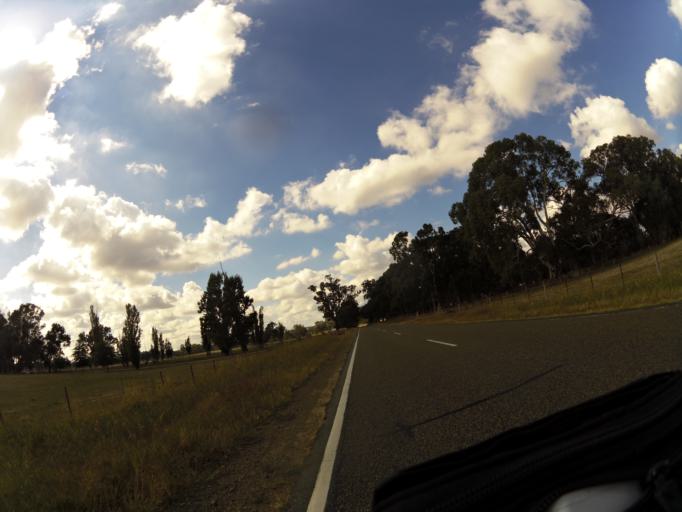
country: AU
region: Victoria
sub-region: Benalla
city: Benalla
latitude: -36.6134
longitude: 146.0243
